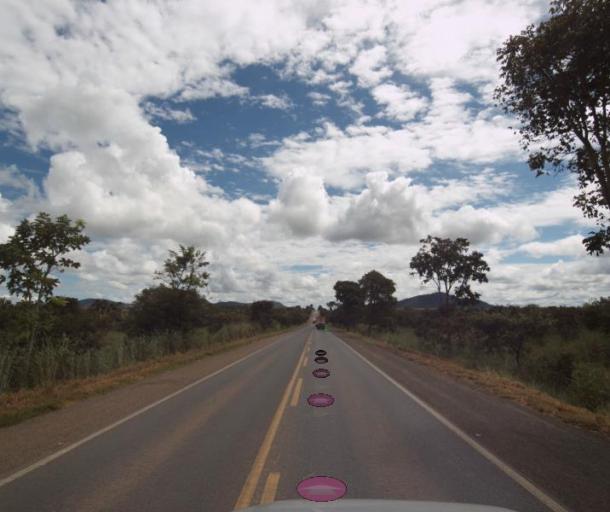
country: BR
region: Goias
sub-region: Uruacu
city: Uruacu
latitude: -14.4473
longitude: -49.1565
